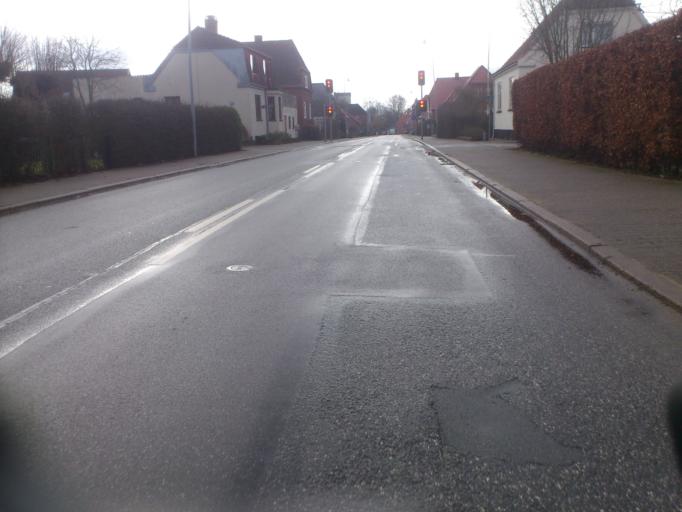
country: DK
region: South Denmark
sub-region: Fredericia Kommune
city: Fredericia
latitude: 55.5724
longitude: 9.7534
